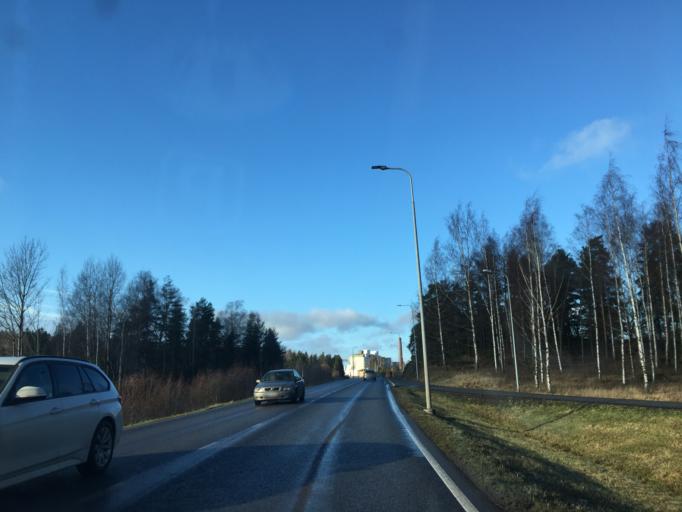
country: FI
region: Varsinais-Suomi
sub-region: Turku
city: Raisio
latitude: 60.4782
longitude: 22.1472
